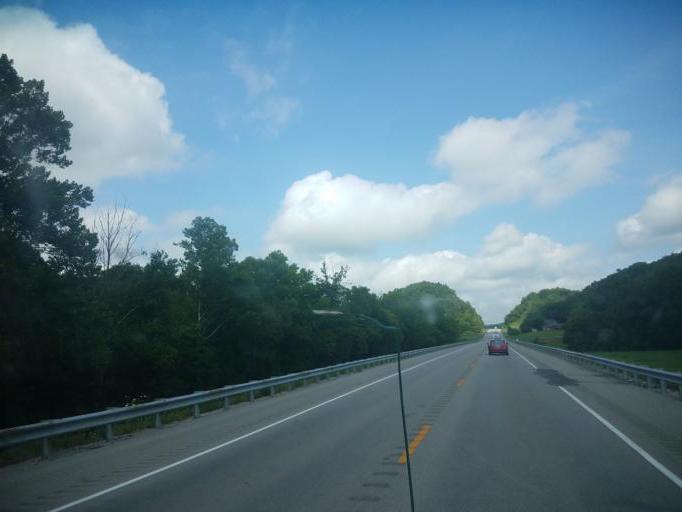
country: US
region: Kentucky
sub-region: Cumberland County
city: Burkesville
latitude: 36.7614
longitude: -85.3353
